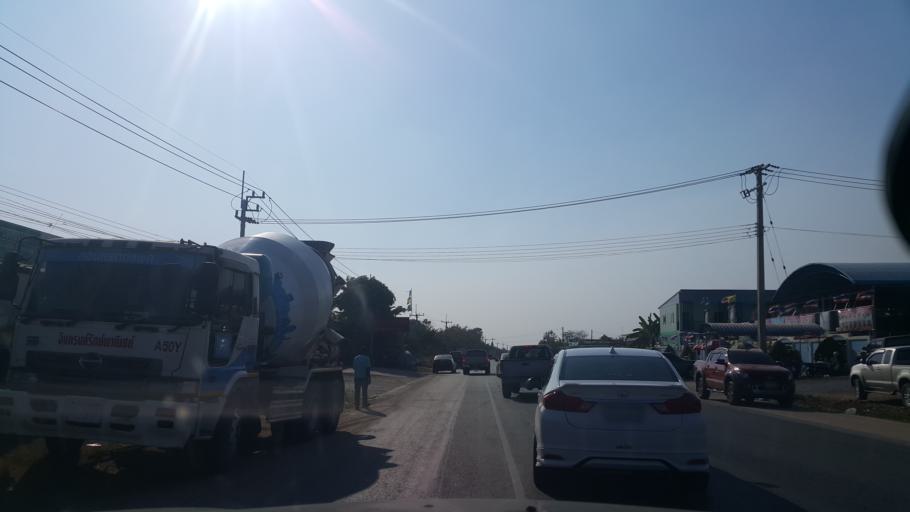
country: TH
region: Nakhon Ratchasima
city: Phimai
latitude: 15.2137
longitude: 102.4799
